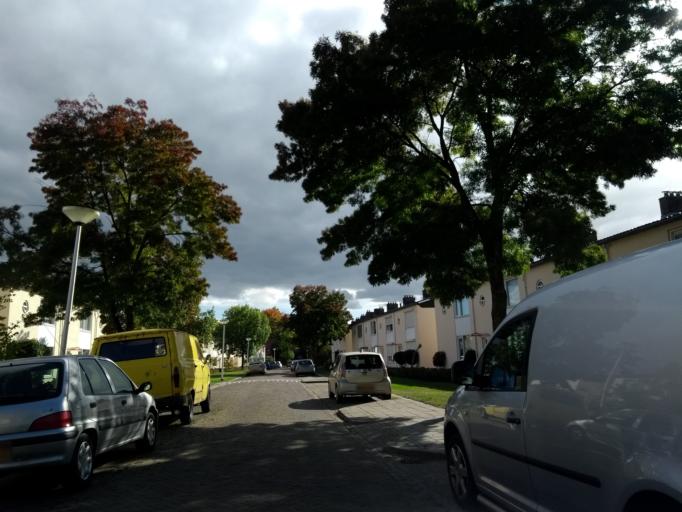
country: NL
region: Overijssel
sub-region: Gemeente Almelo
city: Almelo
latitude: 52.3467
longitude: 6.6758
